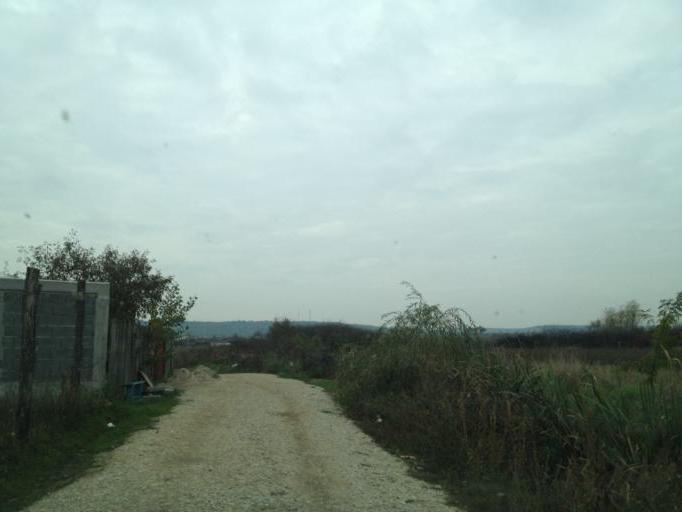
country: RO
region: Dolj
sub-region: Municipiul Craiova
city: Popoveni
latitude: 44.2926
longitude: 23.7802
